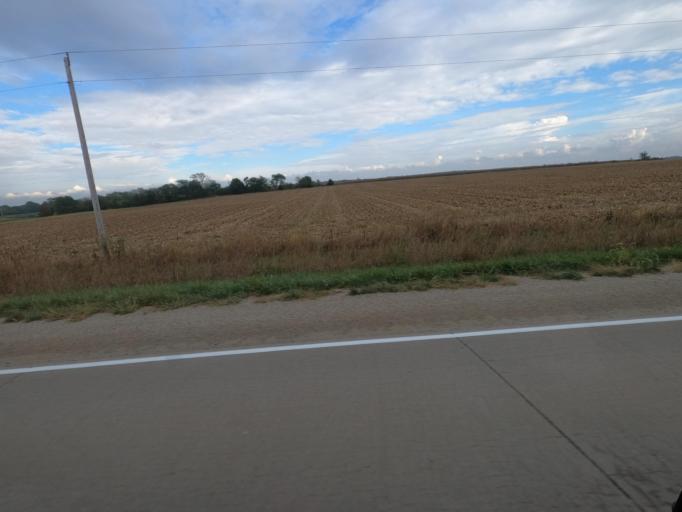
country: US
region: Iowa
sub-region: Henry County
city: Mount Pleasant
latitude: 40.8039
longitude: -91.7043
